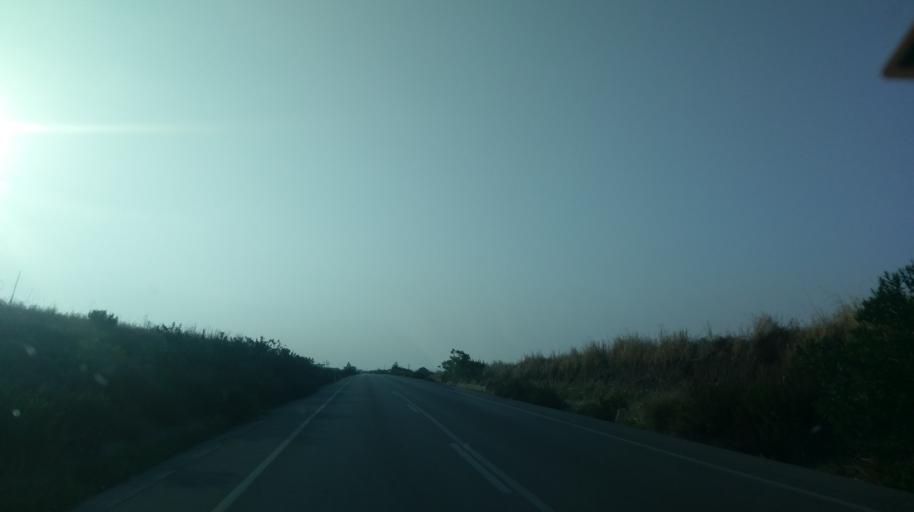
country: CY
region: Ammochostos
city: Trikomo
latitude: 35.4304
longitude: 33.9275
